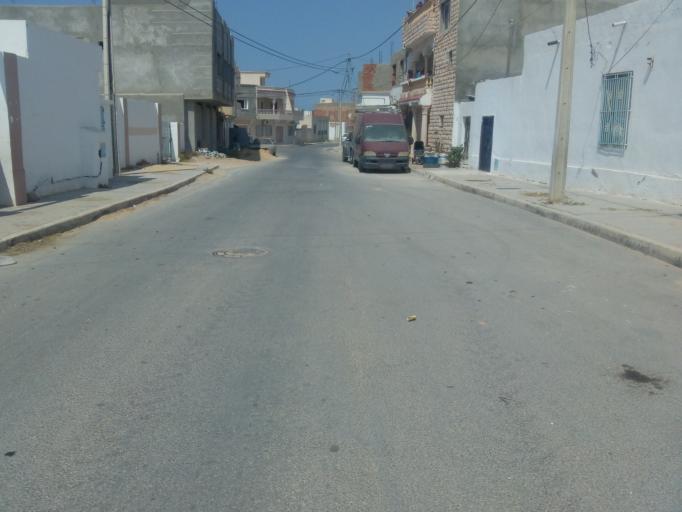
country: TN
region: Qabis
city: Matmata
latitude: 33.6202
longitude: 10.2813
